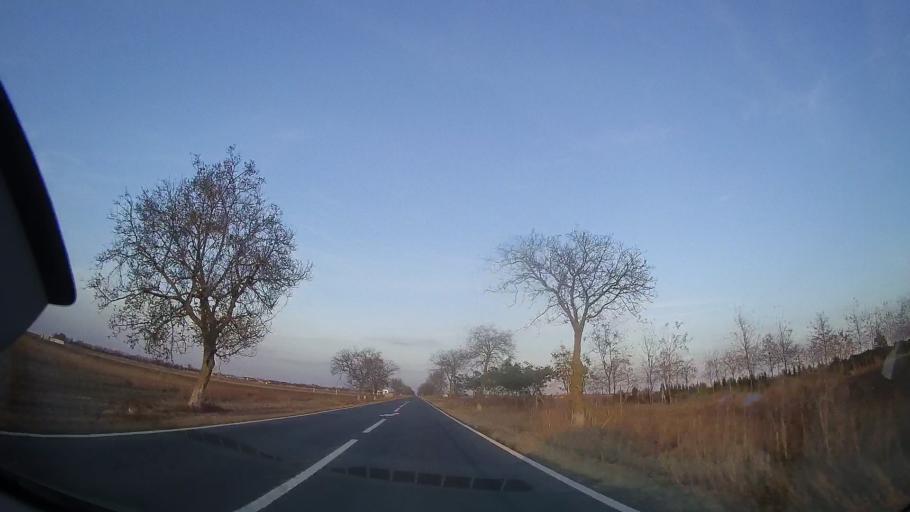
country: RO
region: Constanta
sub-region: Comuna Topraisar
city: Topraisar
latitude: 44.0018
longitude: 28.4361
